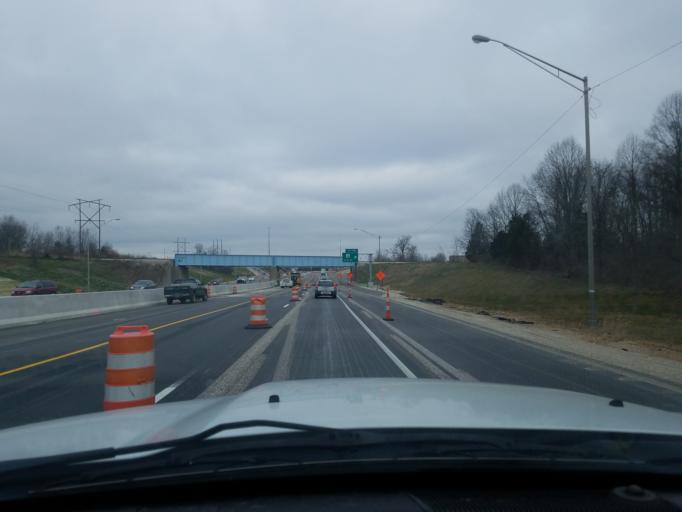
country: US
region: Indiana
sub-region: Monroe County
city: Bloomington
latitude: 39.1596
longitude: -86.5730
